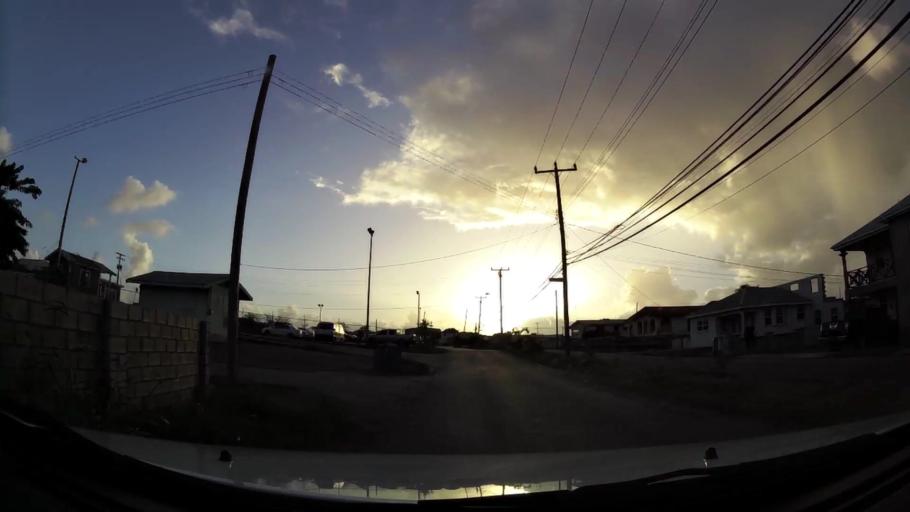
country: BB
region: Saint Philip
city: Crane
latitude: 13.1042
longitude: -59.4698
